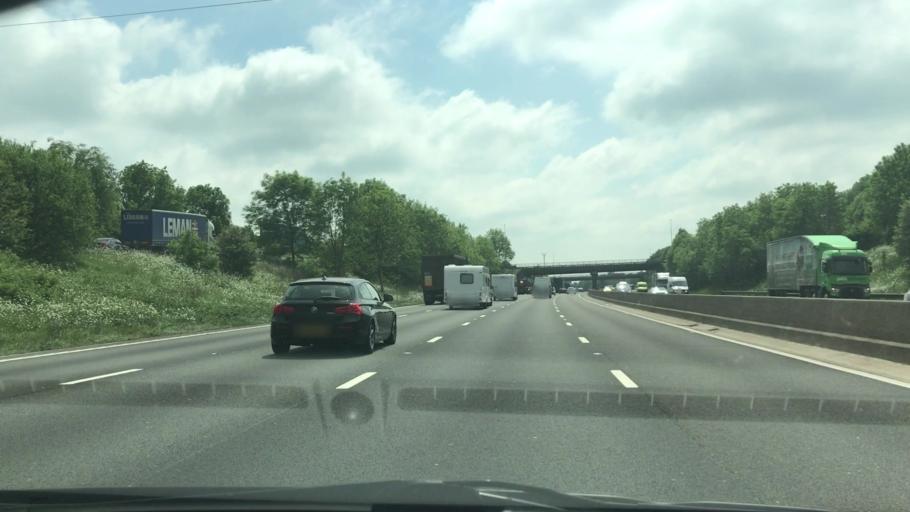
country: GB
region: England
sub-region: Derbyshire
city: Bolsover
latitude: 53.2007
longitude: -1.3219
